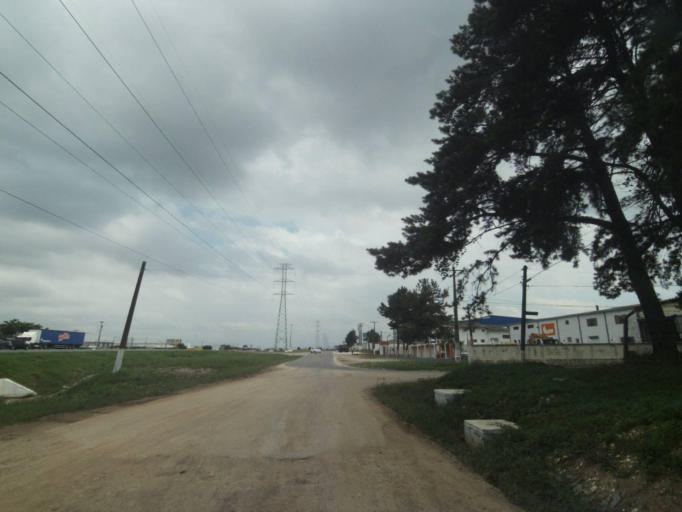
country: BR
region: Parana
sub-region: Curitiba
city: Curitiba
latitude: -25.4756
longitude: -49.3520
